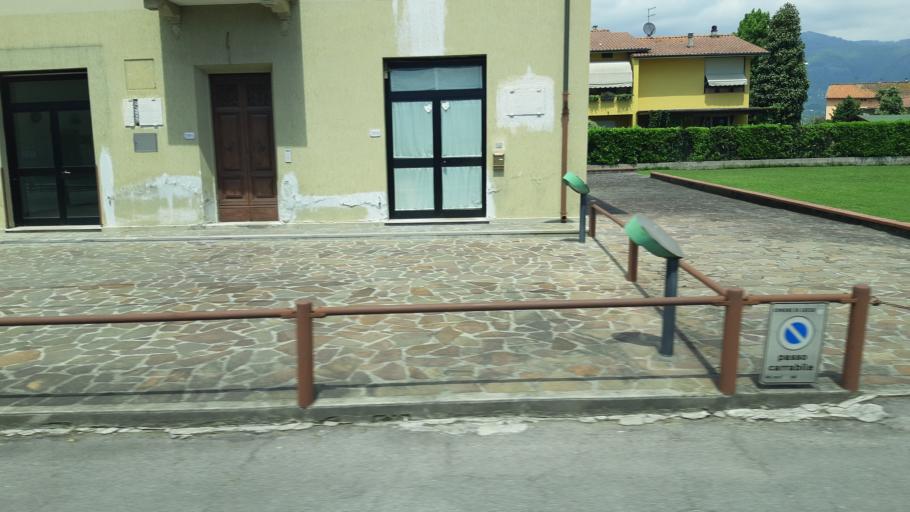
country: IT
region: Tuscany
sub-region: Provincia di Lucca
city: Capannori
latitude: 43.8699
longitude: 10.5403
